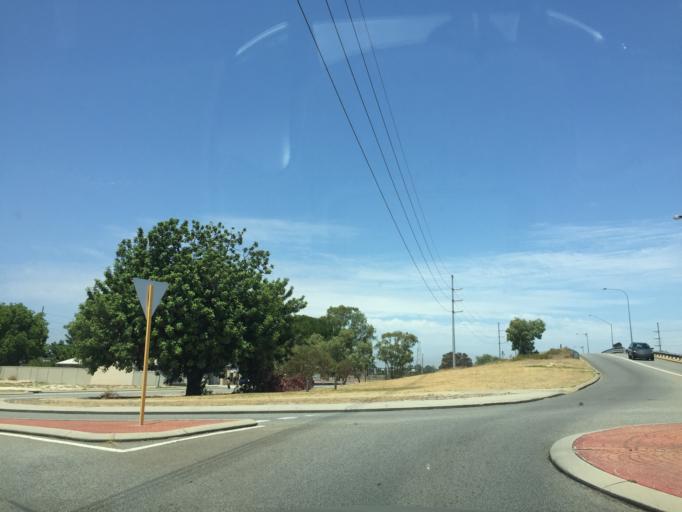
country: AU
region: Western Australia
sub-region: Canning
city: Cannington
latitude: -32.0146
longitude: 115.9483
